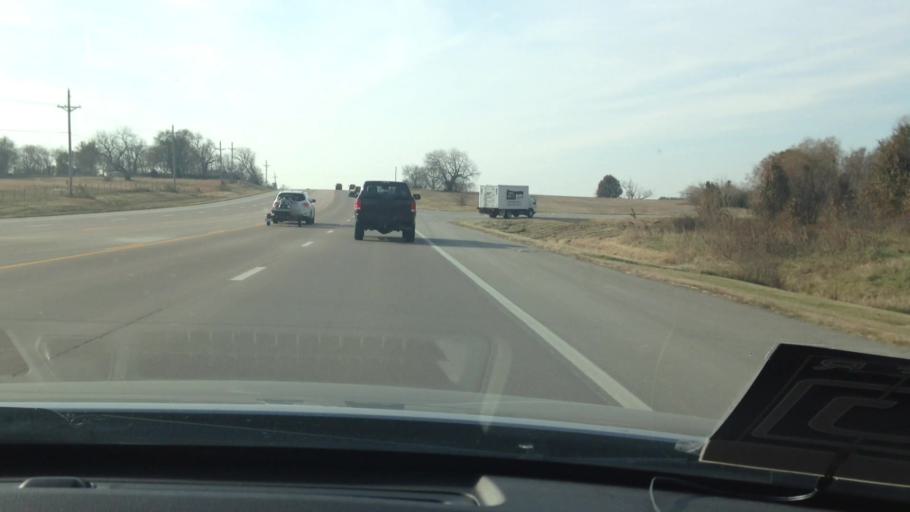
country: US
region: Missouri
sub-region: Henry County
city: Clinton
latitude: 38.3887
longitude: -93.7839
